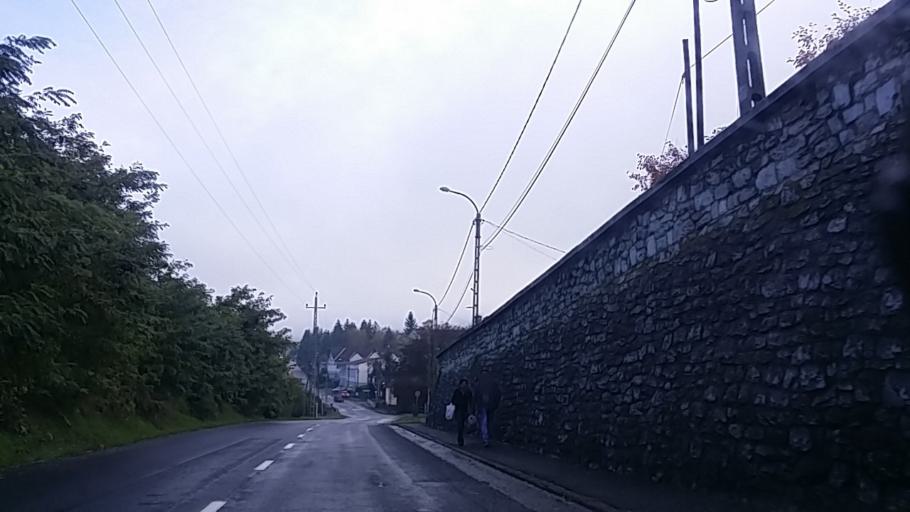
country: HU
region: Heves
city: Belapatfalva
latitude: 48.0509
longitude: 20.3467
